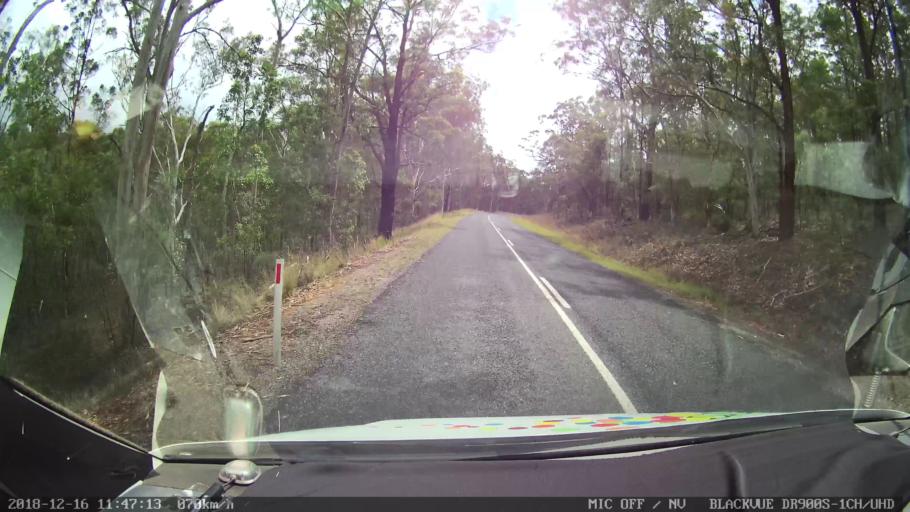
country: AU
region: New South Wales
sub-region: Tenterfield Municipality
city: Carrolls Creek
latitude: -28.9228
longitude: 152.2360
